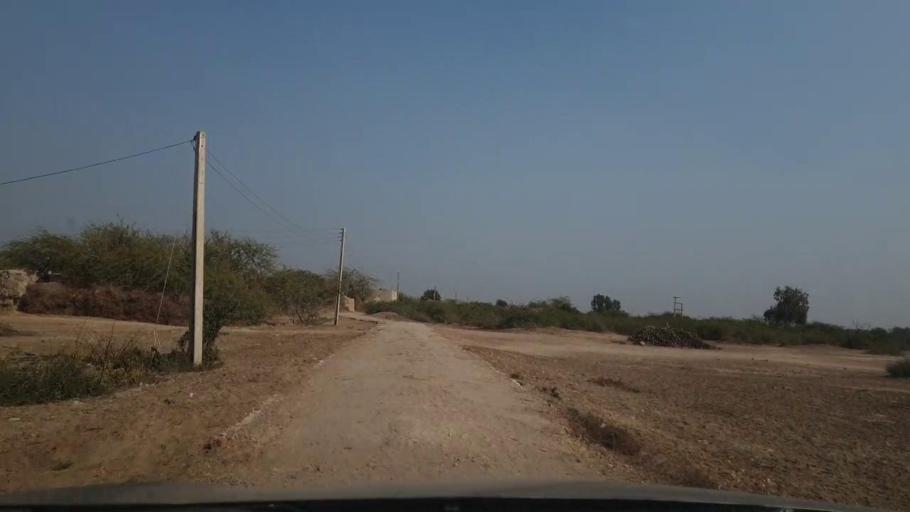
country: PK
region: Sindh
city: Tando Allahyar
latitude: 25.5708
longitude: 68.8183
